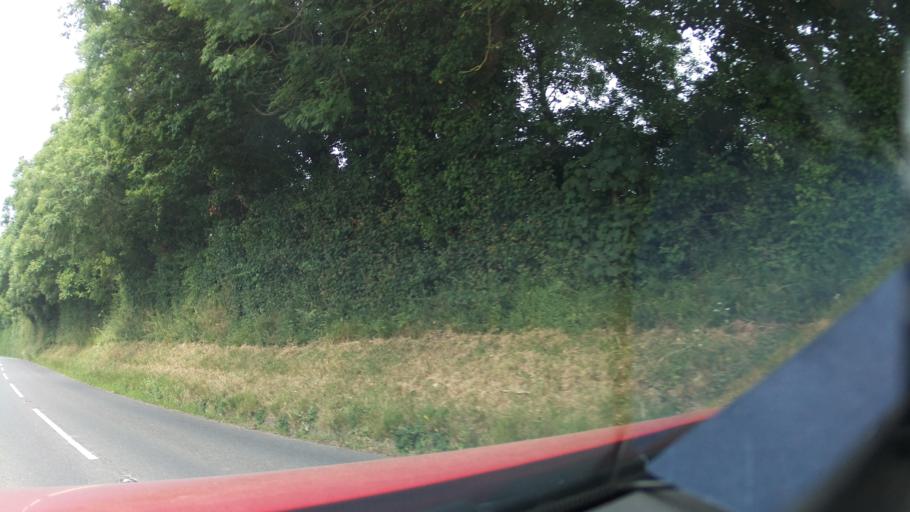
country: GB
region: England
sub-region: Devon
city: Colyton
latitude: 50.7241
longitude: -3.0478
